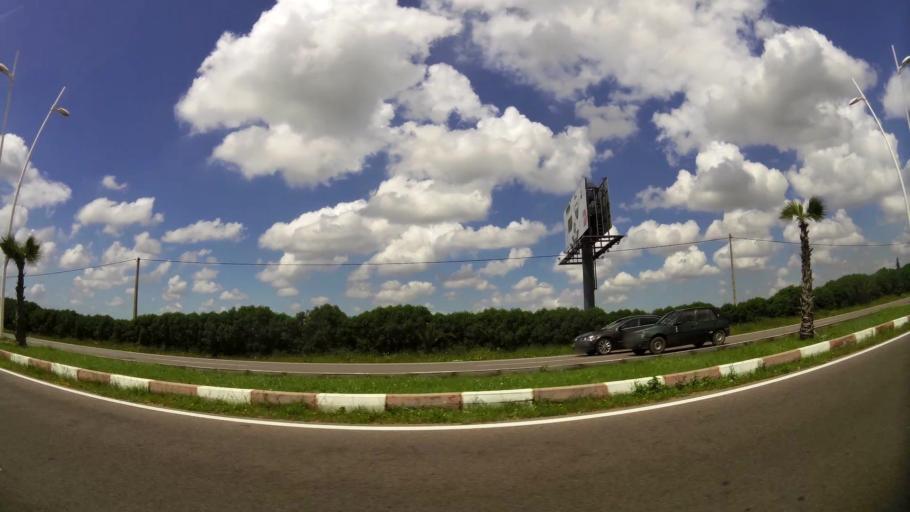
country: MA
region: Chaouia-Ouardigha
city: Nouaseur
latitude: 33.3968
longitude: -7.5862
